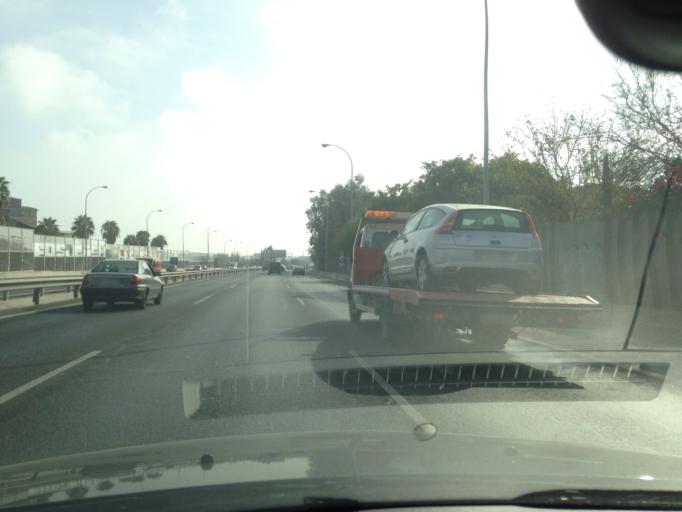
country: ES
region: Andalusia
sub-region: Provincia de Malaga
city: Malaga
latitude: 36.6991
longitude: -4.4584
